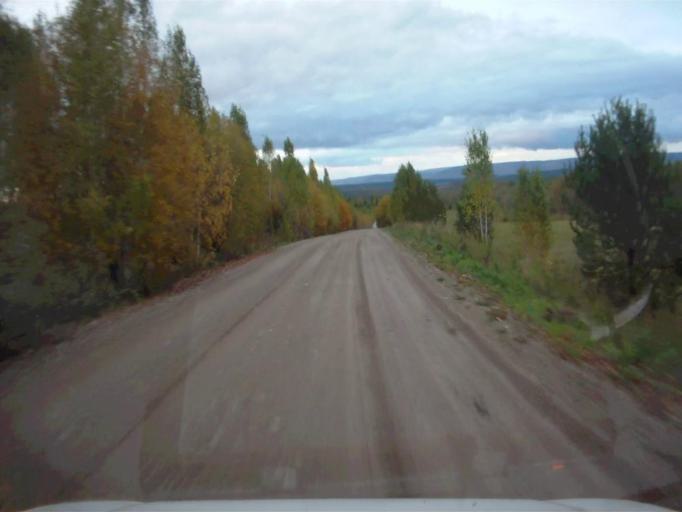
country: RU
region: Sverdlovsk
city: Mikhaylovsk
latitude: 56.2033
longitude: 59.2017
